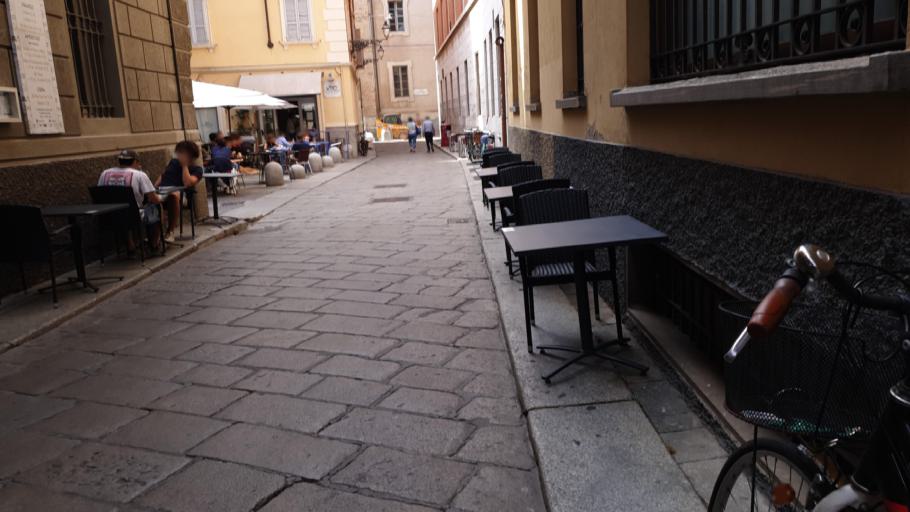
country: IT
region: Emilia-Romagna
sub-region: Provincia di Parma
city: Parma
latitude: 44.8005
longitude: 10.3272
